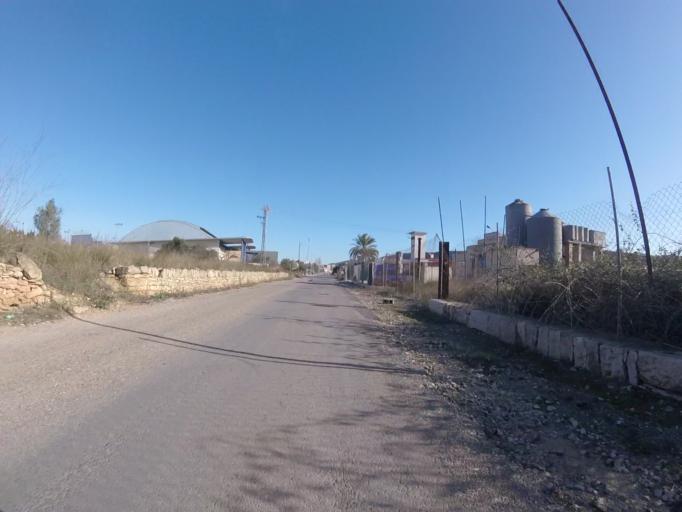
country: ES
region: Valencia
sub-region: Provincia de Castello
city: Alcala de Xivert
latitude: 40.2982
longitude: 0.2204
